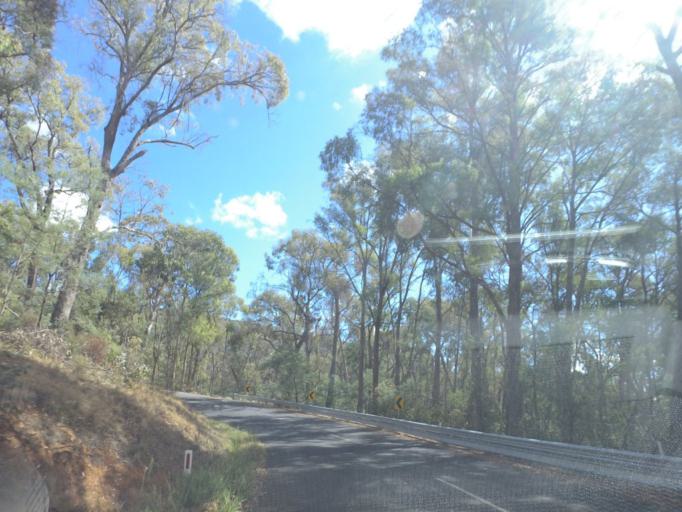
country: AU
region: Victoria
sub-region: Murrindindi
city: Alexandra
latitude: -37.3269
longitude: 145.9427
